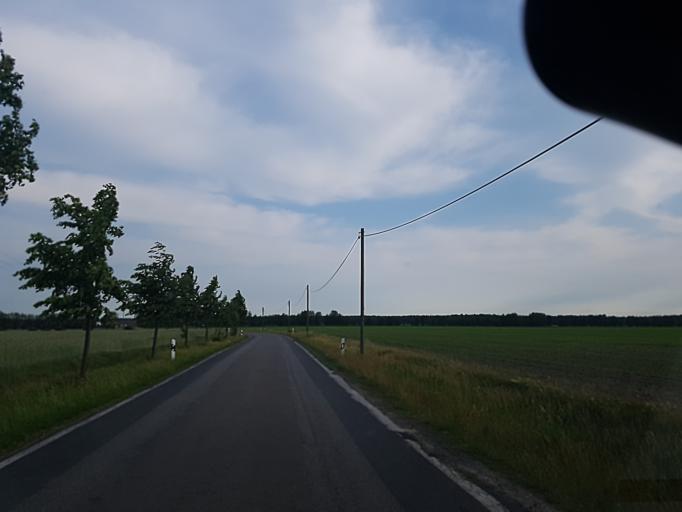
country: DE
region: Saxony-Anhalt
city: Jessen
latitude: 51.8280
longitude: 12.9475
